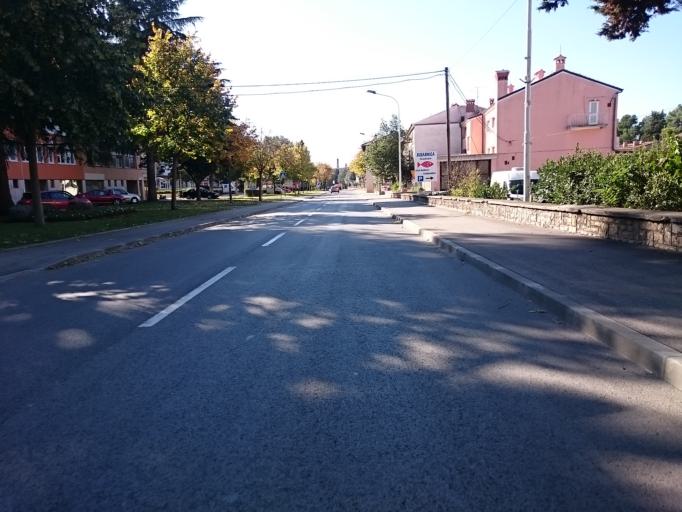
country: HR
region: Istarska
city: Umag
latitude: 45.4357
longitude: 13.5263
